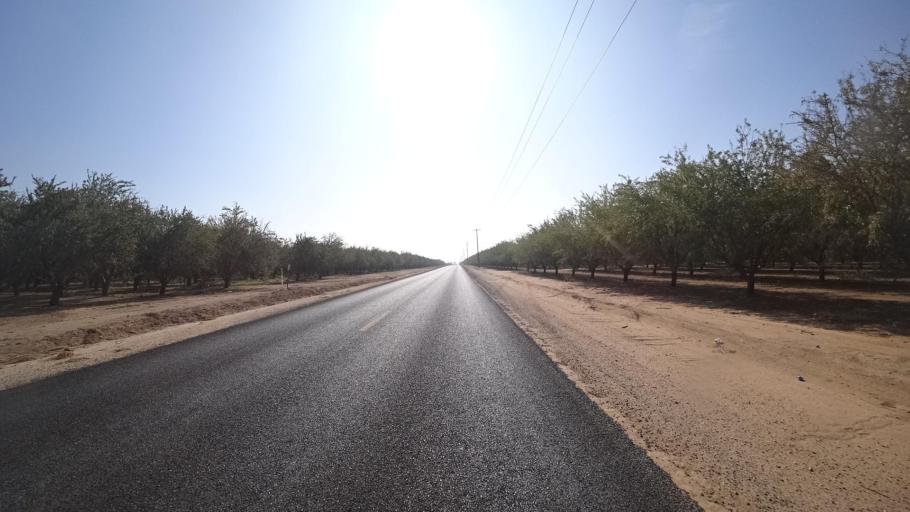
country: US
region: California
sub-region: Kern County
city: Shafter
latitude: 35.5262
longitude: -119.1517
